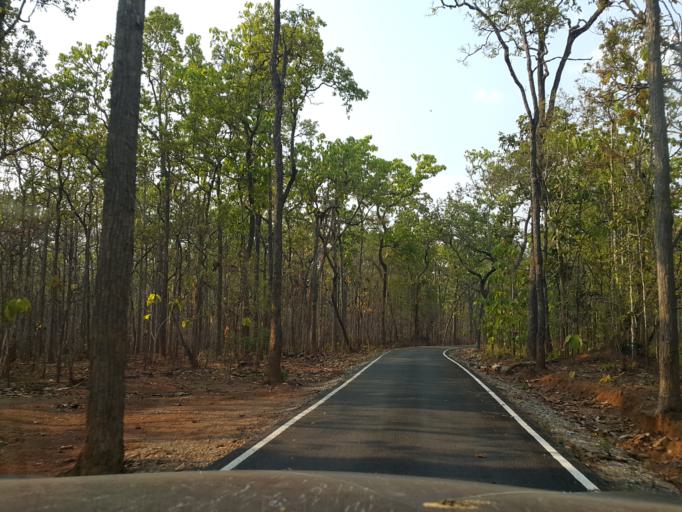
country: TH
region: Lamphun
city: Li
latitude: 17.6238
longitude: 98.8708
